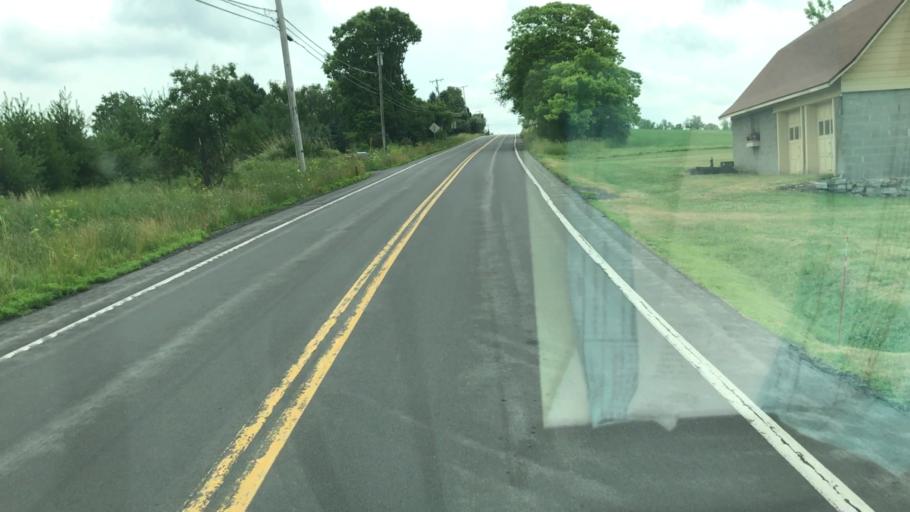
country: US
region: New York
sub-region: Onondaga County
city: Manlius
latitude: 42.9759
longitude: -75.9895
